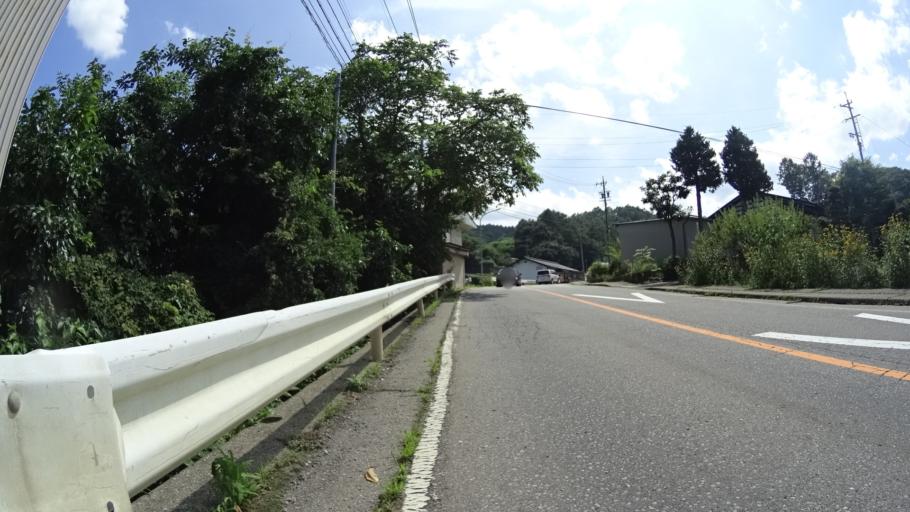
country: JP
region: Nagano
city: Saku
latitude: 36.0593
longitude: 138.4654
